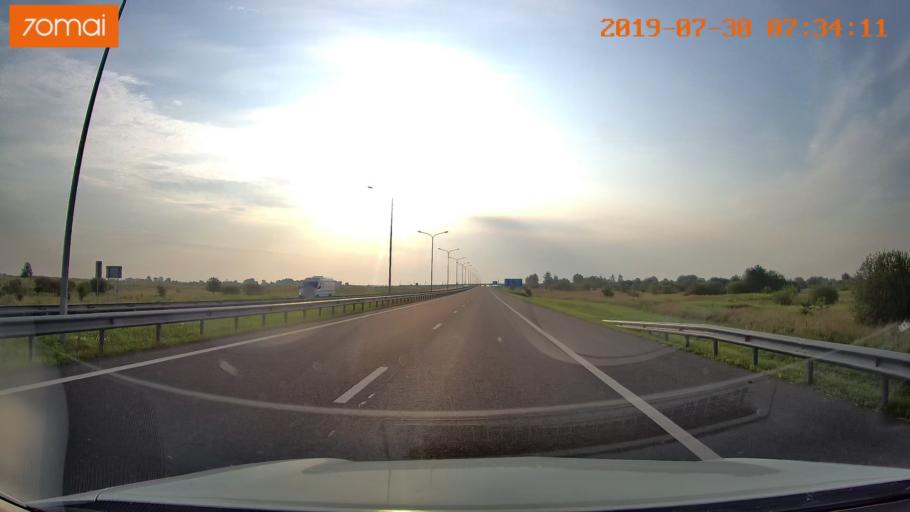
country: RU
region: Kaliningrad
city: Gvardeysk
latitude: 54.6716
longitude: 21.0654
